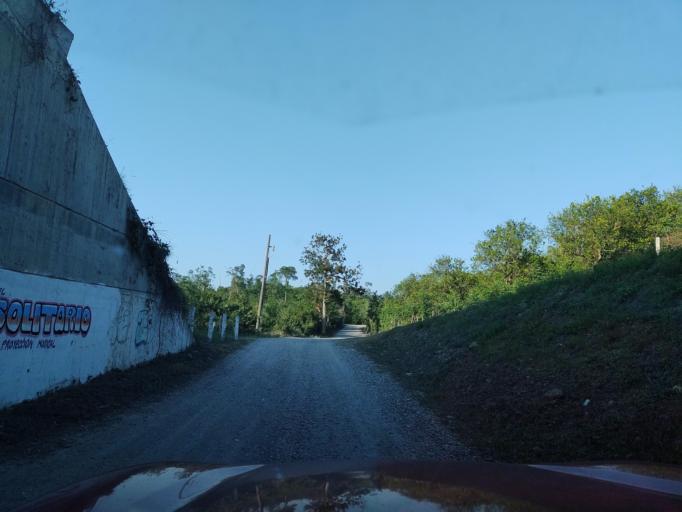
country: MX
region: Veracruz
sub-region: Papantla
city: Polutla
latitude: 20.4512
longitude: -97.2418
